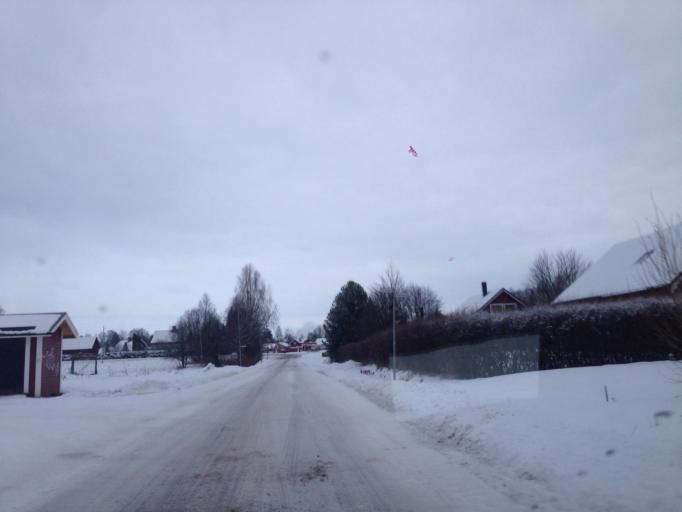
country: SE
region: Dalarna
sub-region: Mora Kommun
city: Mora
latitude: 61.0087
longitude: 14.5825
